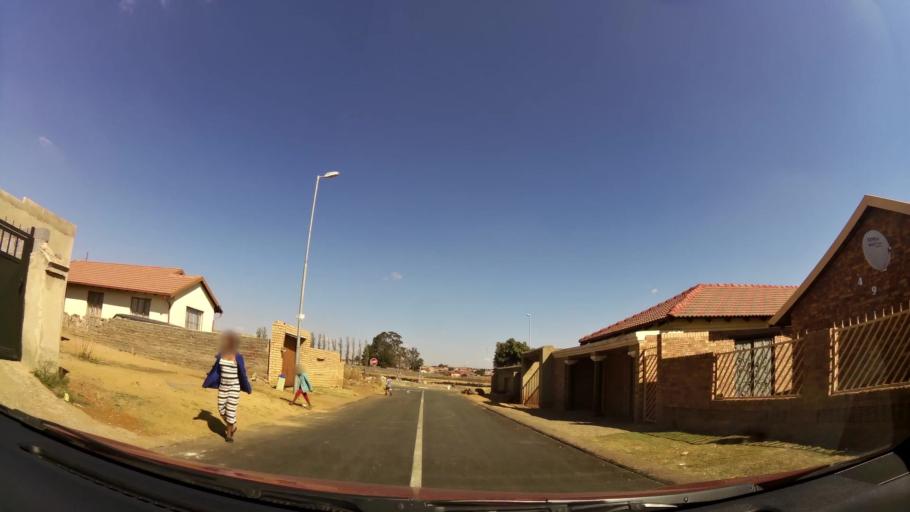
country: ZA
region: Gauteng
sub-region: City of Johannesburg Metropolitan Municipality
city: Soweto
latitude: -26.2376
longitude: 27.8198
